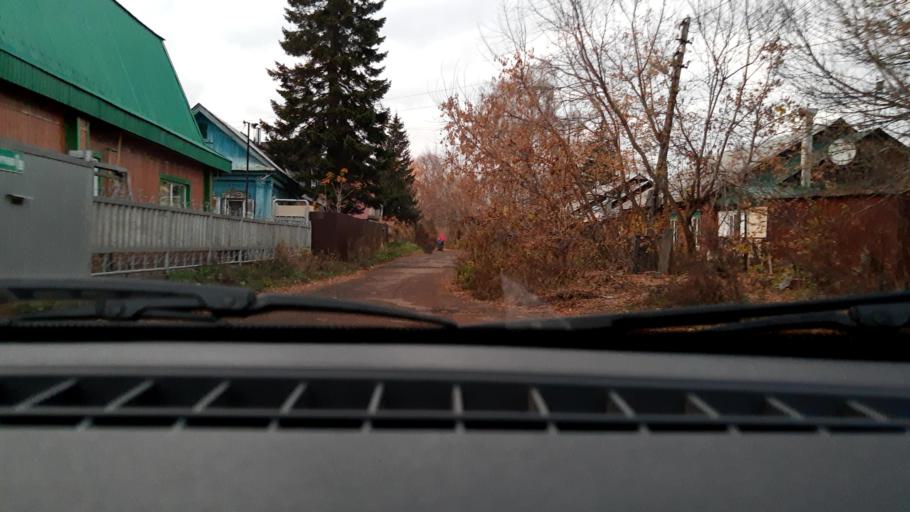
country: RU
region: Bashkortostan
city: Mikhaylovka
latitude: 54.7829
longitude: 55.8838
